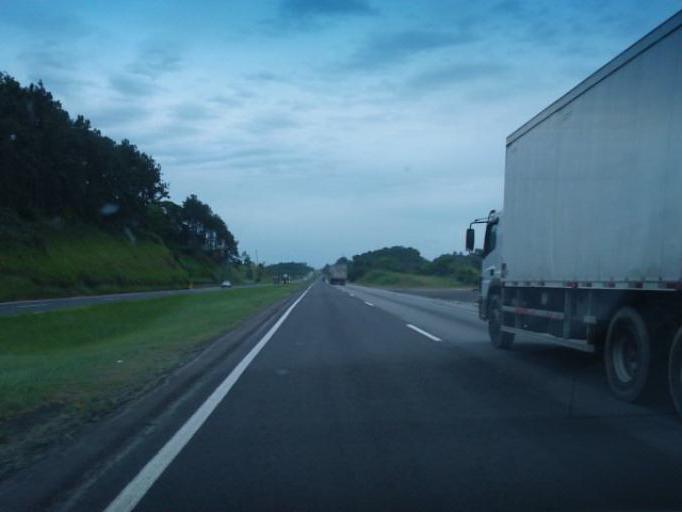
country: BR
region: Sao Paulo
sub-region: Registro
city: Registro
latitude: -24.4274
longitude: -47.7834
